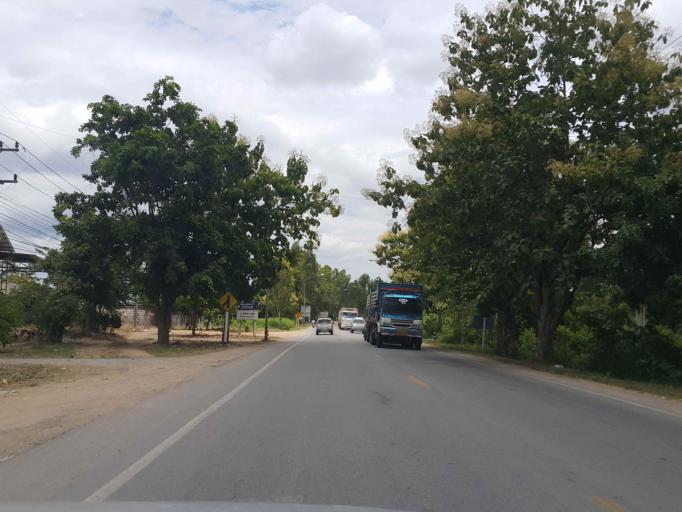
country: TH
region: Lamphun
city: Pa Sang
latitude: 18.4510
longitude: 98.8912
